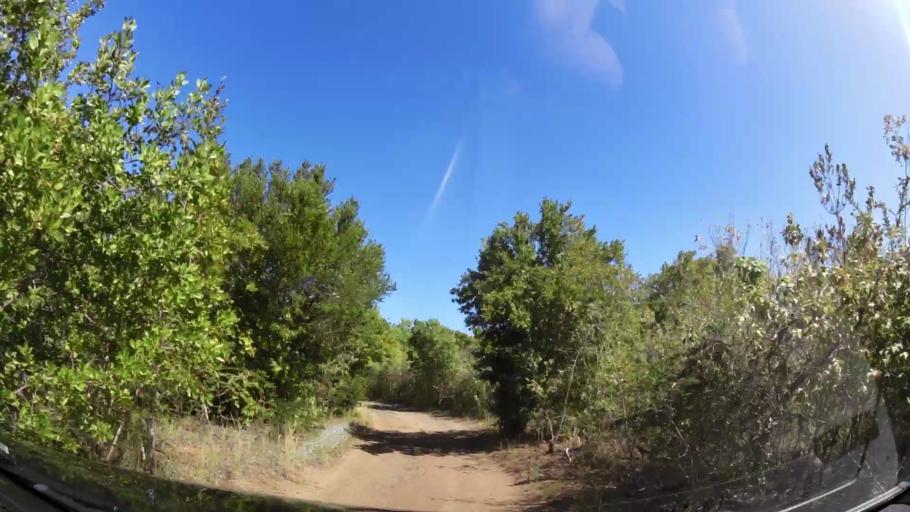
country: VG
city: Tortola
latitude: 18.4446
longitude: -64.5311
